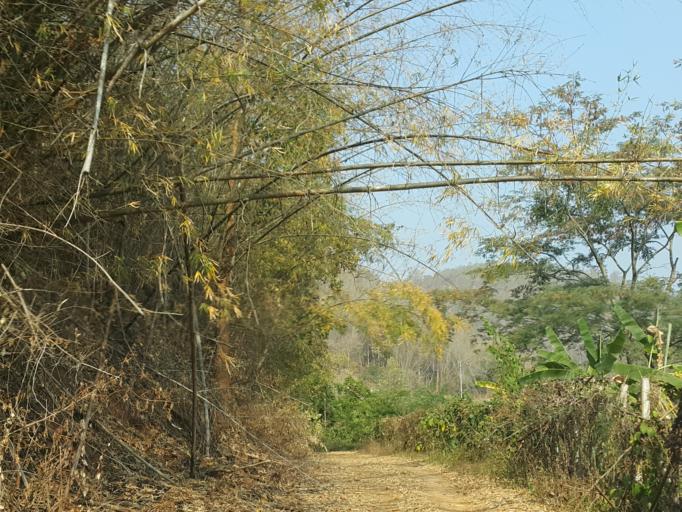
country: TH
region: Chiang Mai
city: Hang Dong
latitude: 18.7408
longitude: 98.8596
